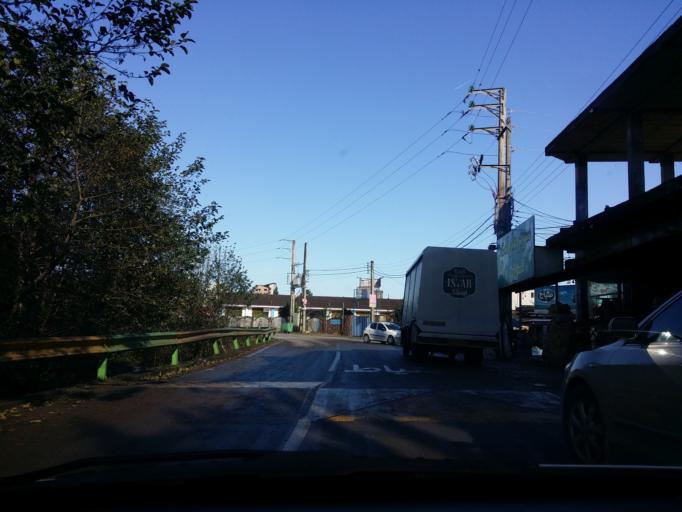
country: IR
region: Mazandaran
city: Chalus
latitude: 36.6858
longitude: 51.3134
